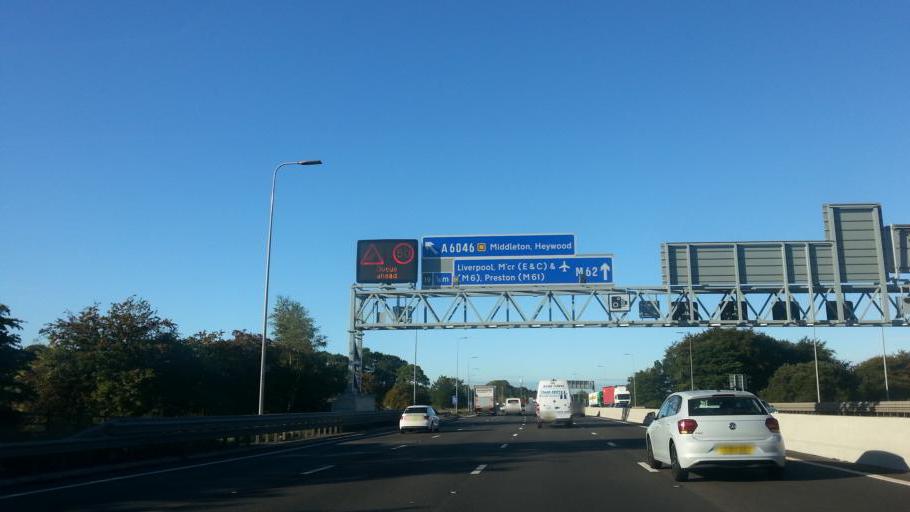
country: GB
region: England
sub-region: Manchester
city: Heywood
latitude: 53.5817
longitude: -2.1954
